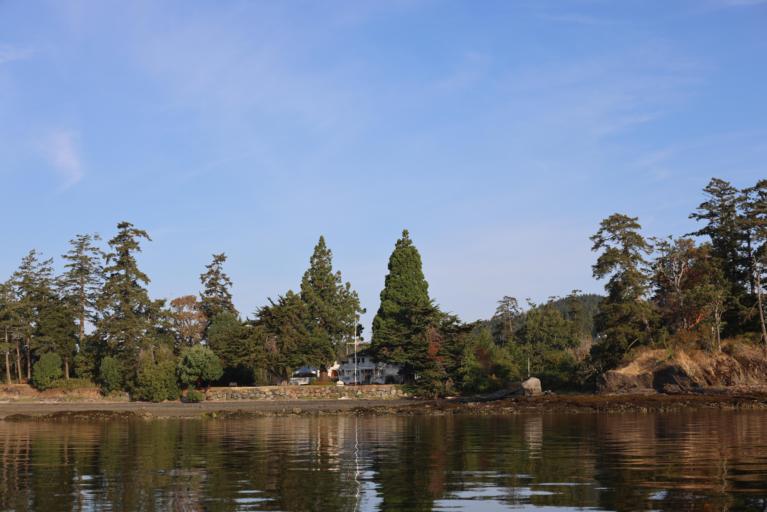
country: CA
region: British Columbia
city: North Saanich
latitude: 48.6747
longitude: -123.4132
